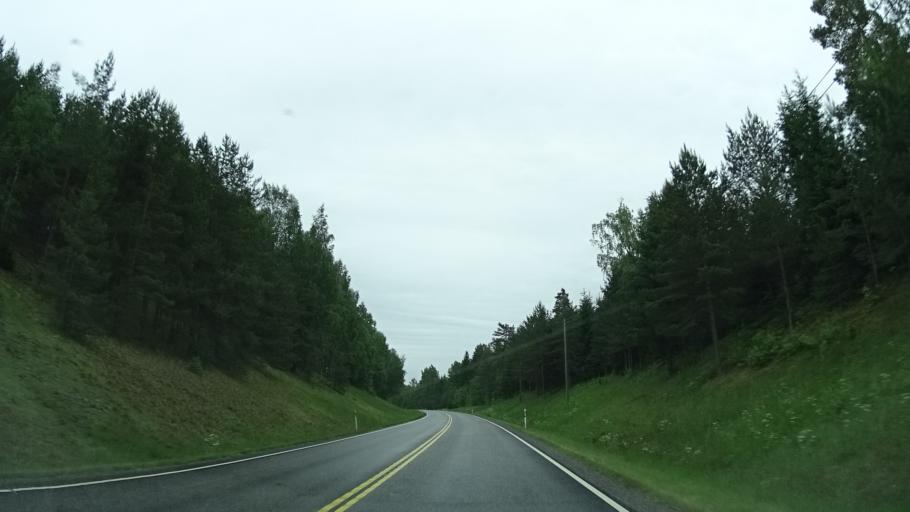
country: FI
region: Varsinais-Suomi
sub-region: Salo
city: Pernioe
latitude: 60.0828
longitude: 23.2353
